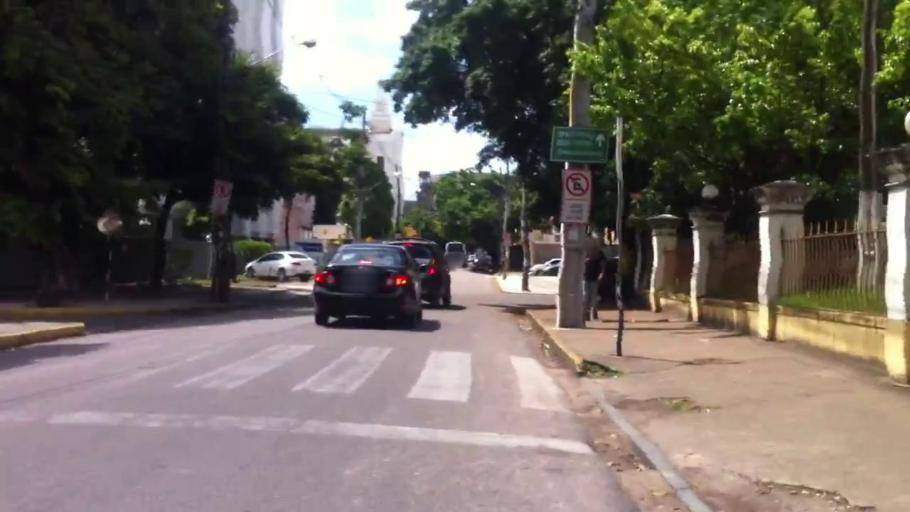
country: BR
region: Pernambuco
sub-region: Recife
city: Recife
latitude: -8.0549
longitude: -34.8909
